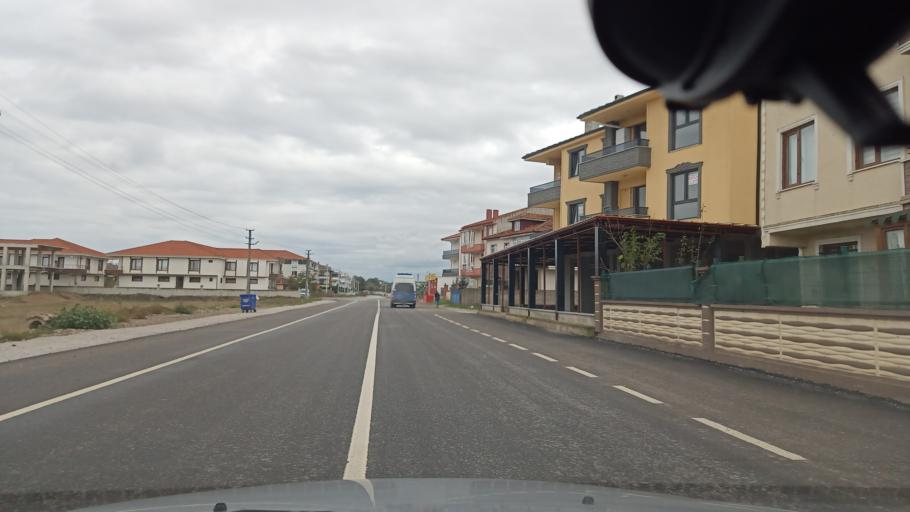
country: TR
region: Sakarya
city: Karasu
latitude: 41.1149
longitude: 30.6709
